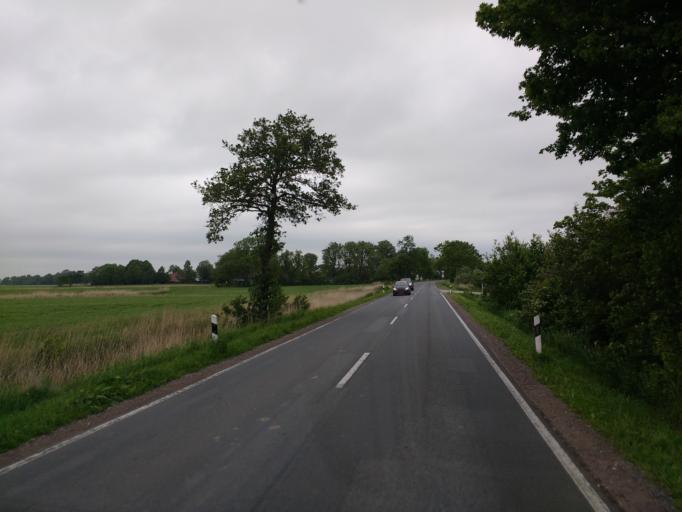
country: DE
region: Lower Saxony
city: Jever
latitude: 53.5928
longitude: 7.9172
